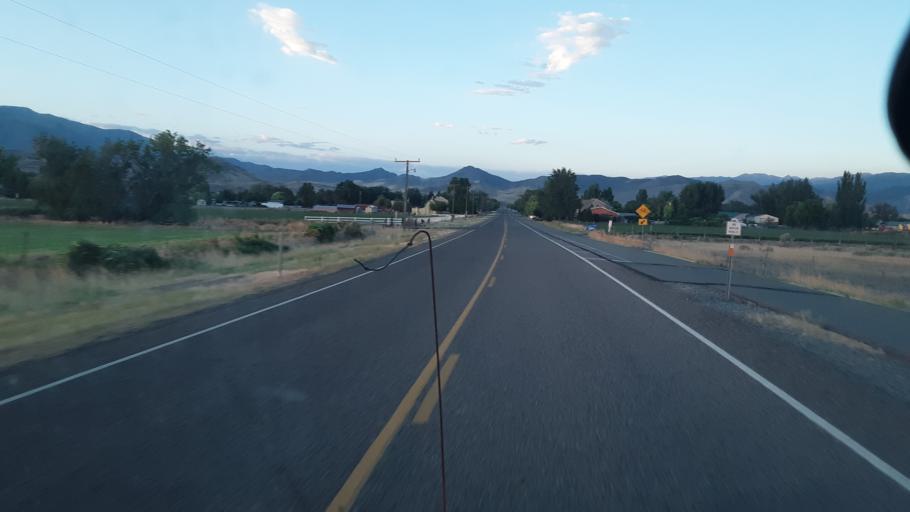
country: US
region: Utah
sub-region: Sevier County
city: Monroe
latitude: 38.6321
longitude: -112.2179
